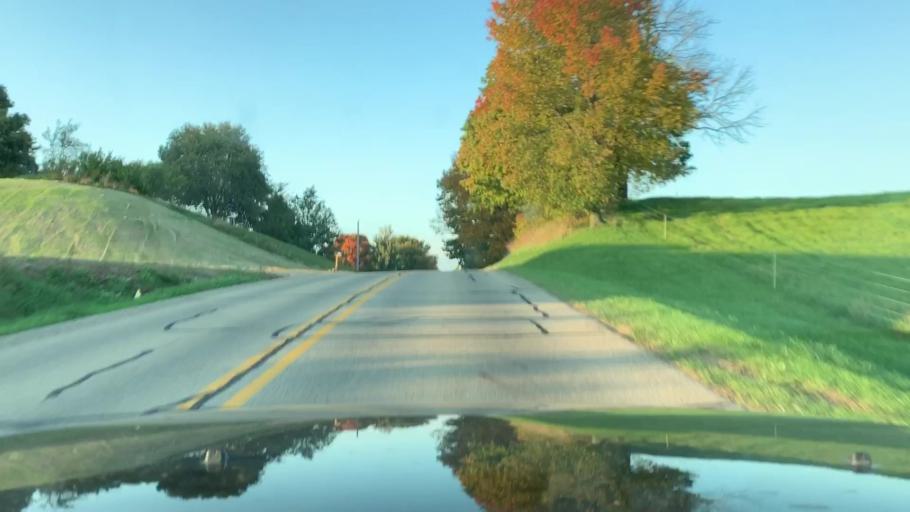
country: US
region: Michigan
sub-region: Kent County
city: Byron Center
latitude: 42.8148
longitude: -85.8026
